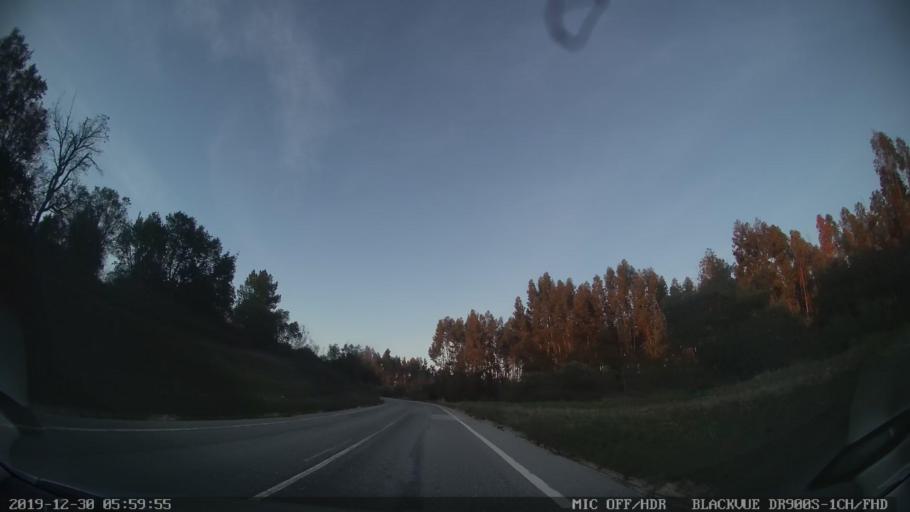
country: PT
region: Castelo Branco
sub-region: Idanha-A-Nova
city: Idanha-a-Nova
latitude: 40.0480
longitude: -7.2437
